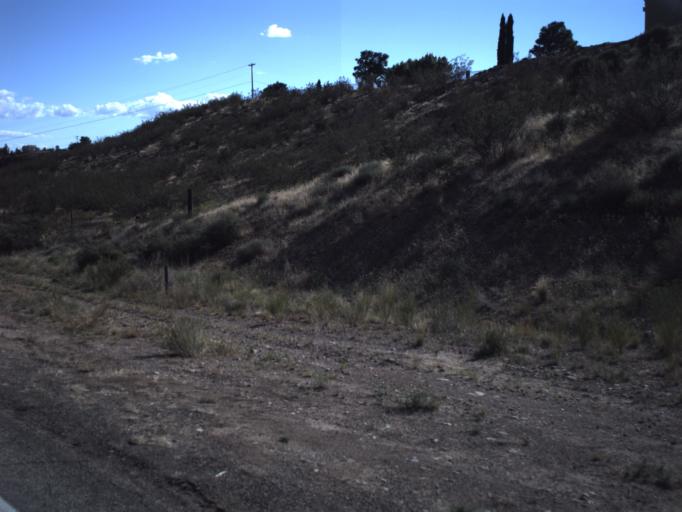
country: US
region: Utah
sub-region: Washington County
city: Toquerville
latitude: 37.2293
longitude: -113.2807
